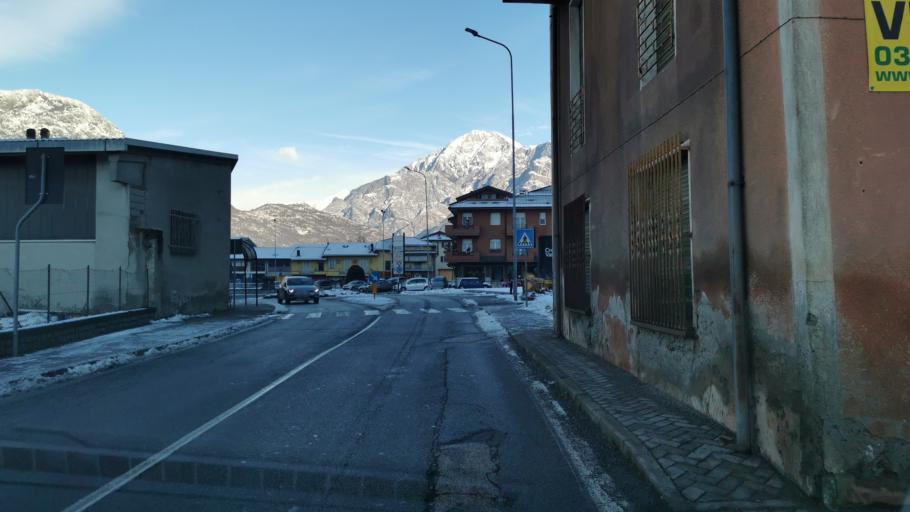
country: IT
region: Lombardy
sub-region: Provincia di Sondrio
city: Dubino
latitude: 46.1706
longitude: 9.4326
